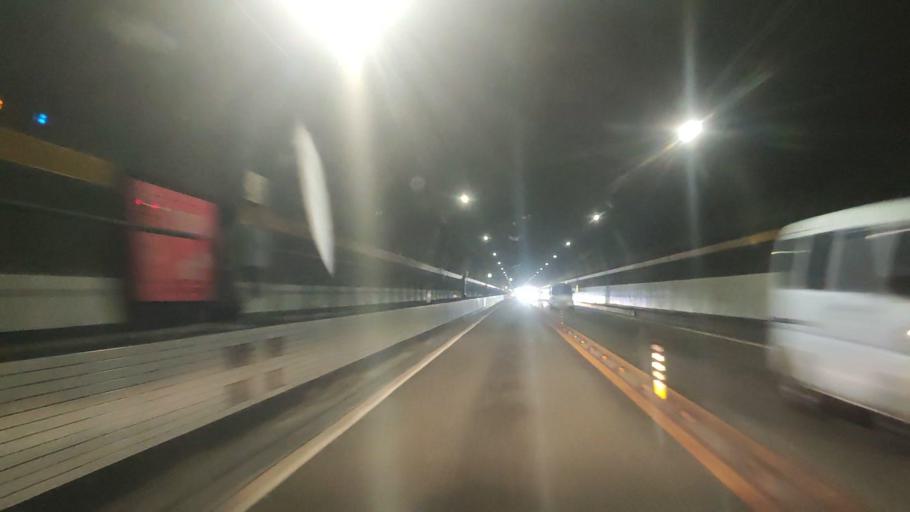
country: JP
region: Nagasaki
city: Nagasaki-shi
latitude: 32.7778
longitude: 129.8878
